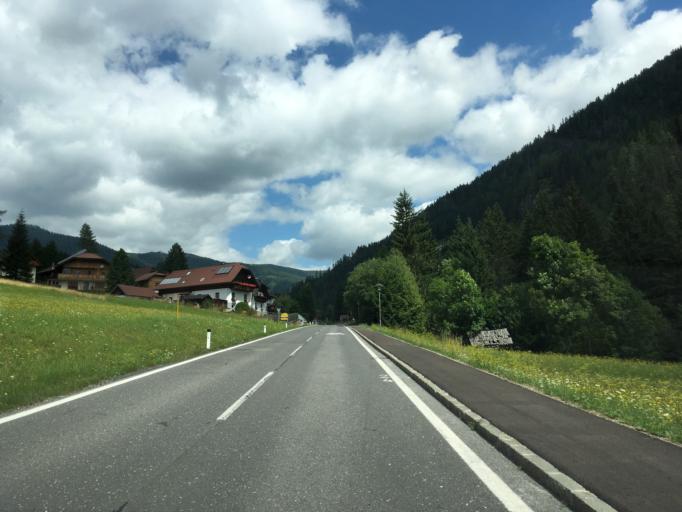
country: AT
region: Carinthia
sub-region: Politischer Bezirk Spittal an der Drau
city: Kleinkirchheim
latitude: 46.8236
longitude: 13.7705
